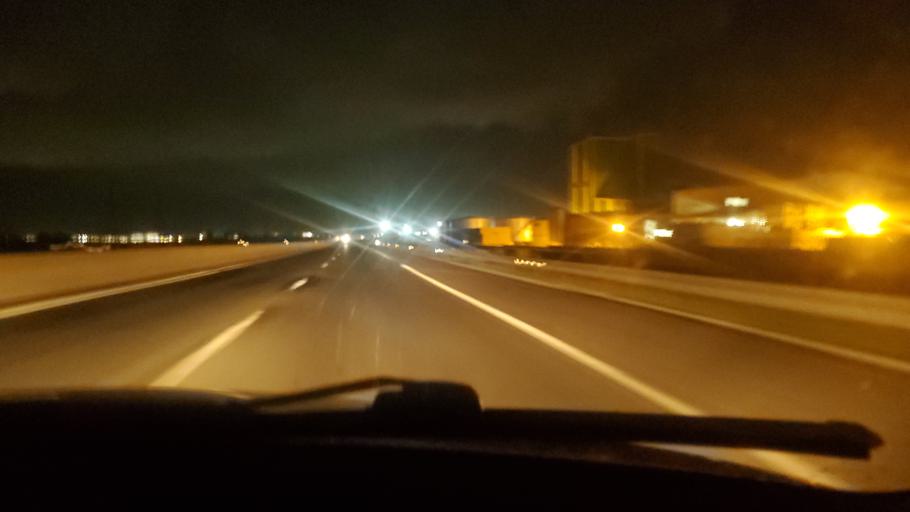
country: SN
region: Dakar
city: Pikine
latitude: 14.7327
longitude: -17.2435
